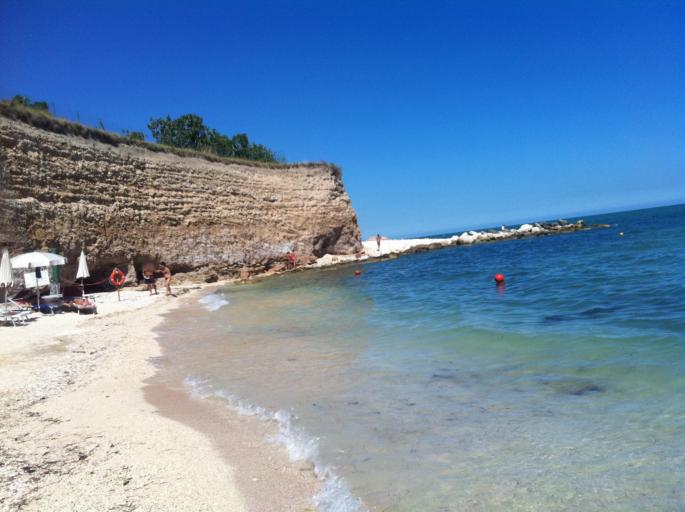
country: IT
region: Apulia
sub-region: Provincia di Foggia
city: Monte Sant'Angelo
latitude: 41.6556
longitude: 15.9781
